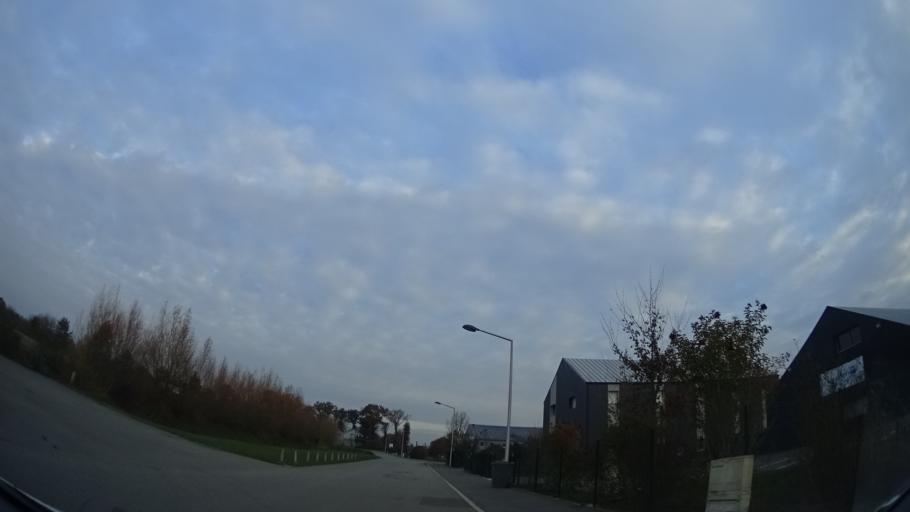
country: FR
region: Brittany
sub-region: Departement d'Ille-et-Vilaine
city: La Chapelle-des-Fougeretz
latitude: 48.1908
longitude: -1.7327
